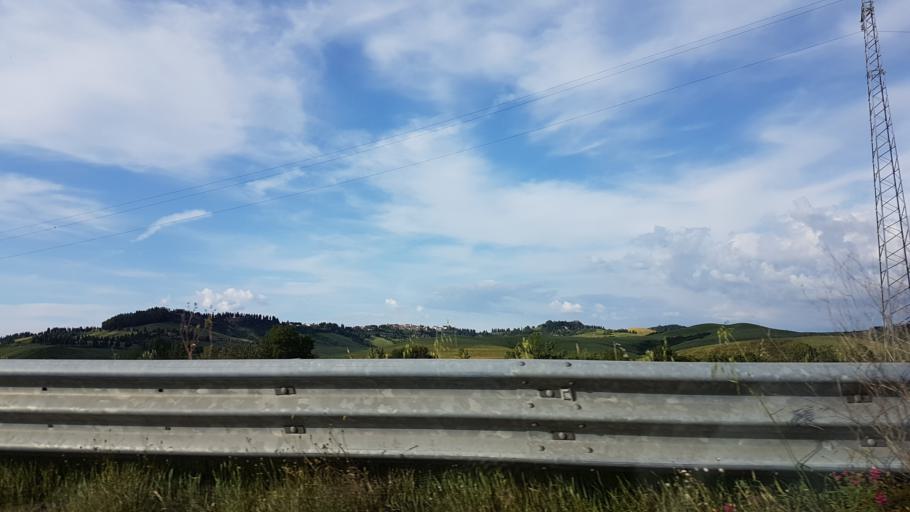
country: IT
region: Tuscany
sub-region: Province of Pisa
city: Lajatico
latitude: 43.4873
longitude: 10.7450
